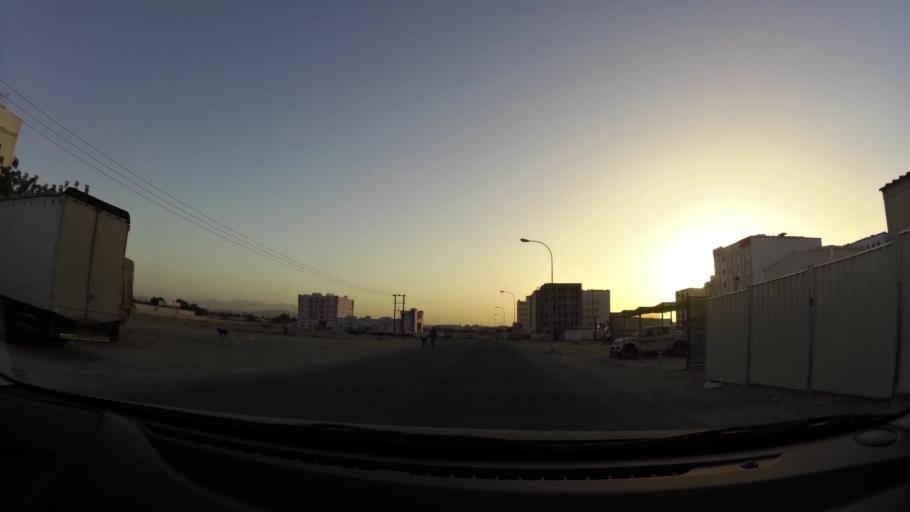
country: OM
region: Muhafazat Masqat
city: As Sib al Jadidah
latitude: 23.5925
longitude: 58.2357
